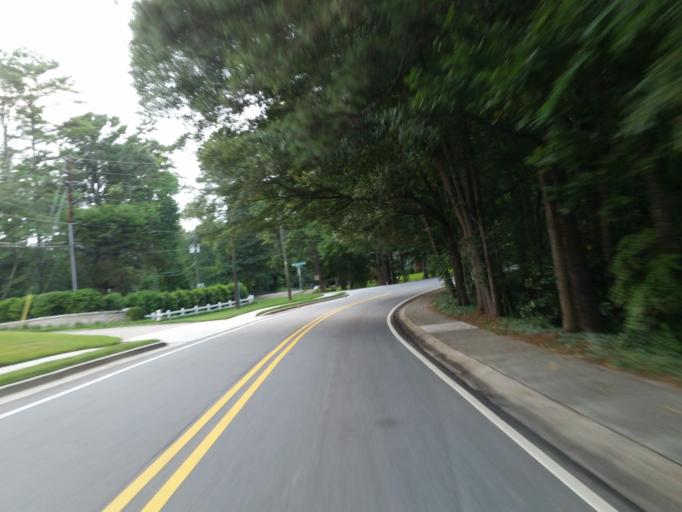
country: US
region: Georgia
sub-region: Cobb County
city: Vinings
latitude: 33.8614
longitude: -84.4617
